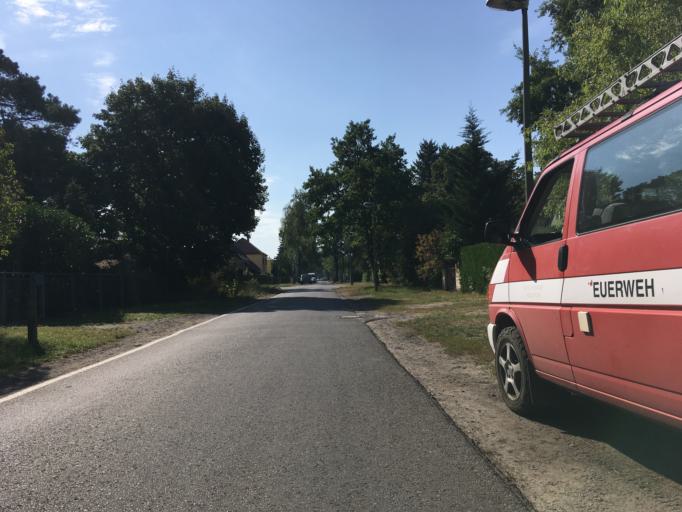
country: DE
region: Berlin
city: Mahlsdorf
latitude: 52.4866
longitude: 13.6074
